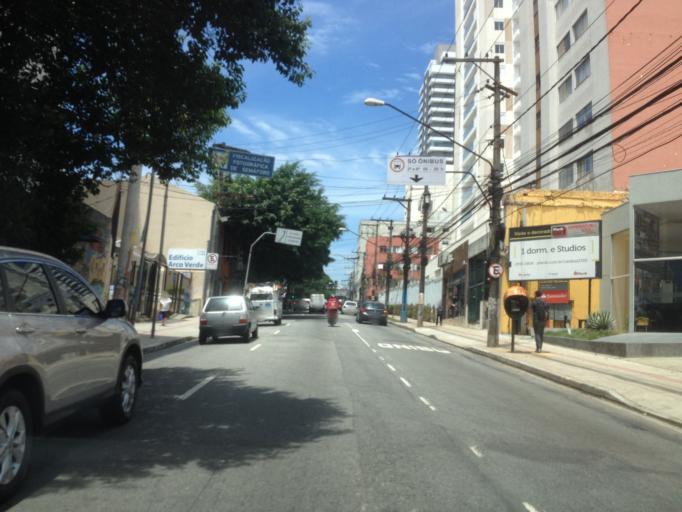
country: BR
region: Sao Paulo
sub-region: Sao Paulo
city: Sao Paulo
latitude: -23.5613
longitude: -46.6878
